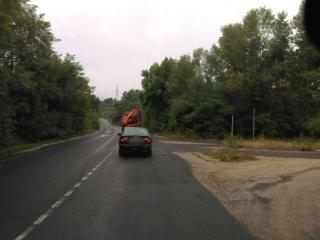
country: BG
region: Plovdiv
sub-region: Obshtina Karlovo
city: Karlovo
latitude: 42.5372
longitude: 24.8171
